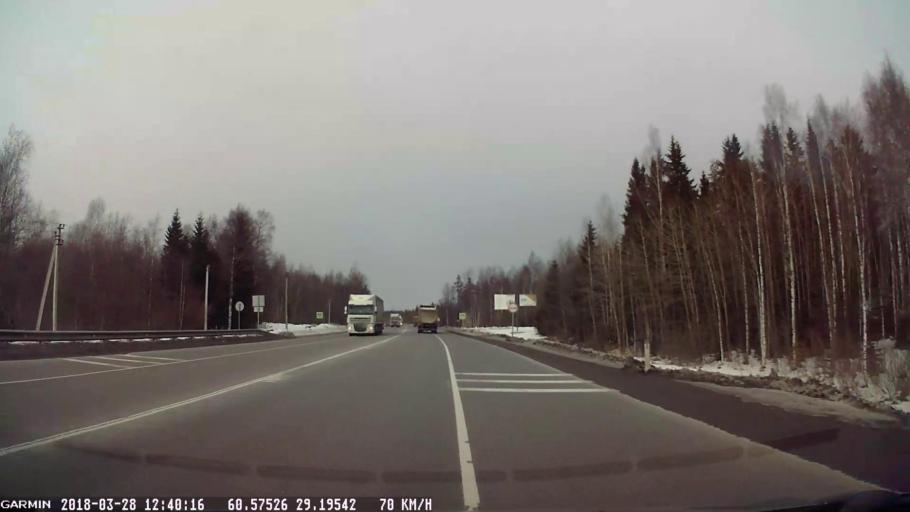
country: RU
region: Leningrad
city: Veshchevo
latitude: 60.5753
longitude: 29.1953
